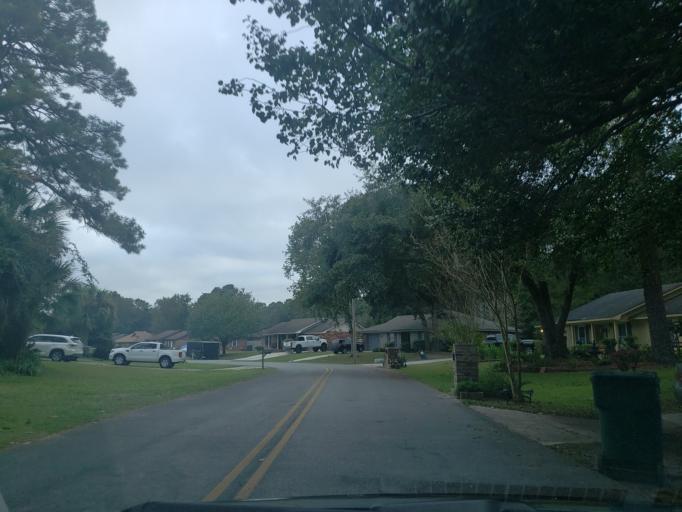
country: US
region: Georgia
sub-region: Chatham County
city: Montgomery
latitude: 31.9539
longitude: -81.1114
